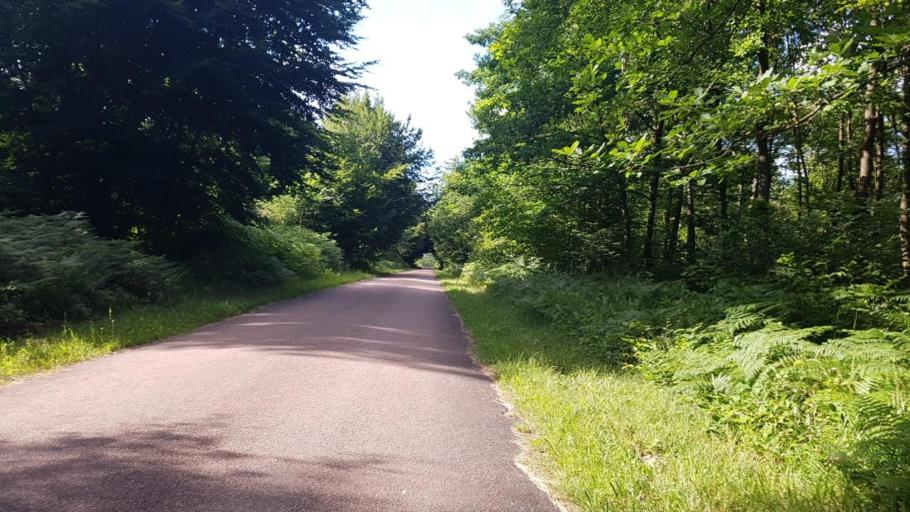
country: FR
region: Picardie
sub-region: Departement de l'Oise
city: Chamant
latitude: 49.1648
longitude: 2.6341
